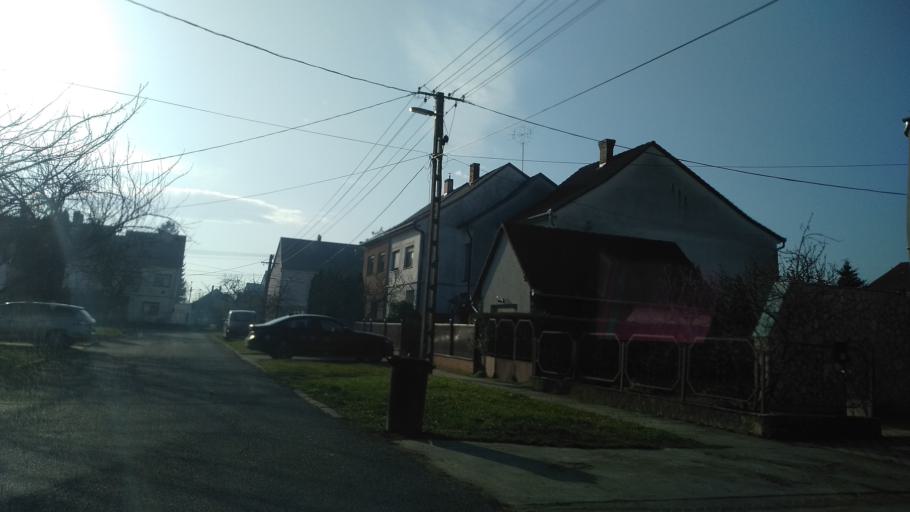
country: HU
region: Somogy
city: Barcs
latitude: 45.9612
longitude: 17.4728
